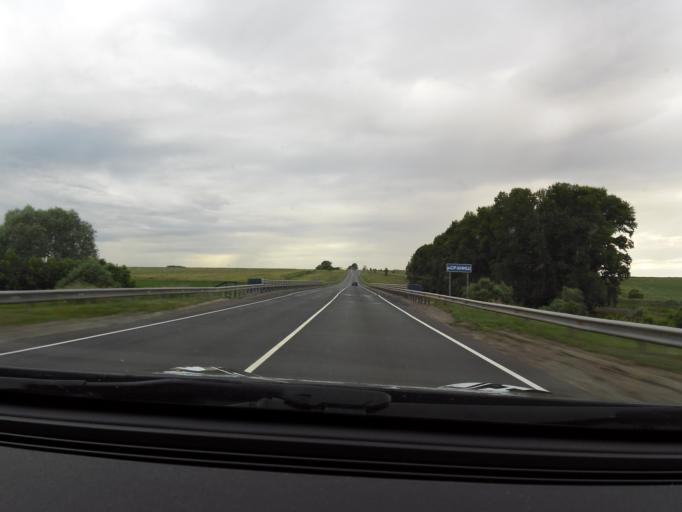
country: RU
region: Chuvashia
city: Yantikovo
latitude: 55.8082
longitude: 47.9659
